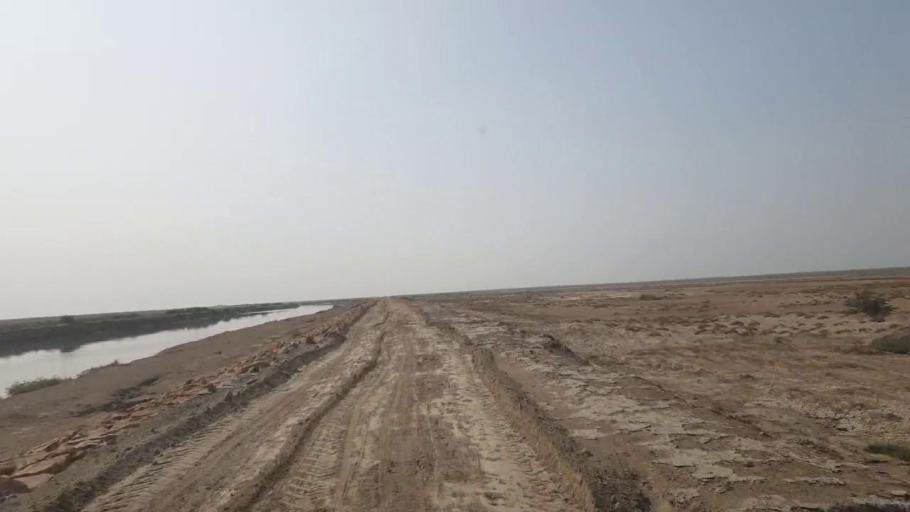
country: PK
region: Sindh
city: Kadhan
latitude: 24.3384
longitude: 68.8517
